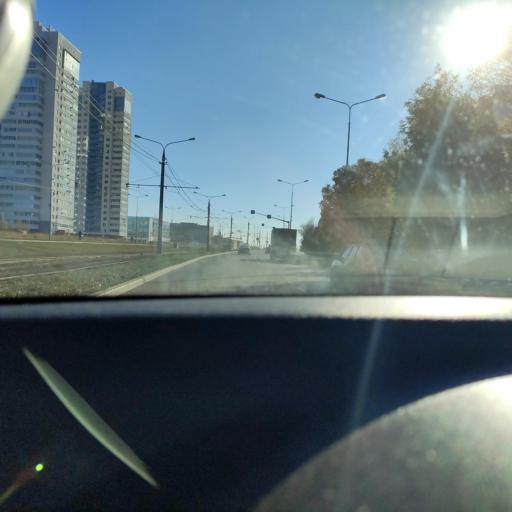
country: RU
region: Samara
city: Samara
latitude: 53.2668
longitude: 50.2285
